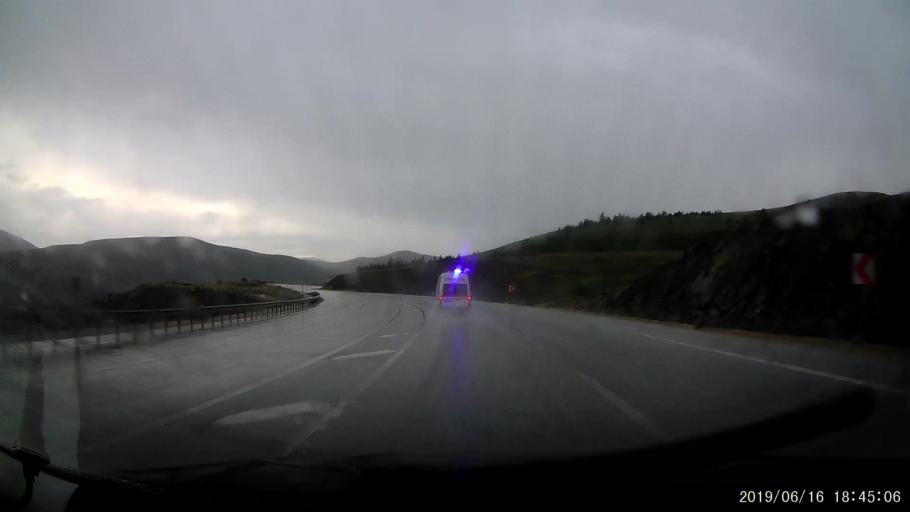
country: TR
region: Erzincan
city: Doganbeyli
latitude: 39.8722
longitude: 39.0625
